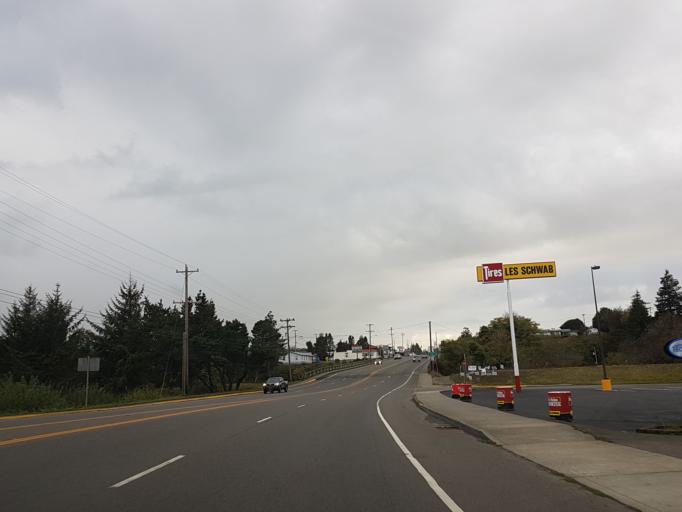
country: US
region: Oregon
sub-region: Douglas County
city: Reedsport
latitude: 43.6976
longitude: -124.1130
